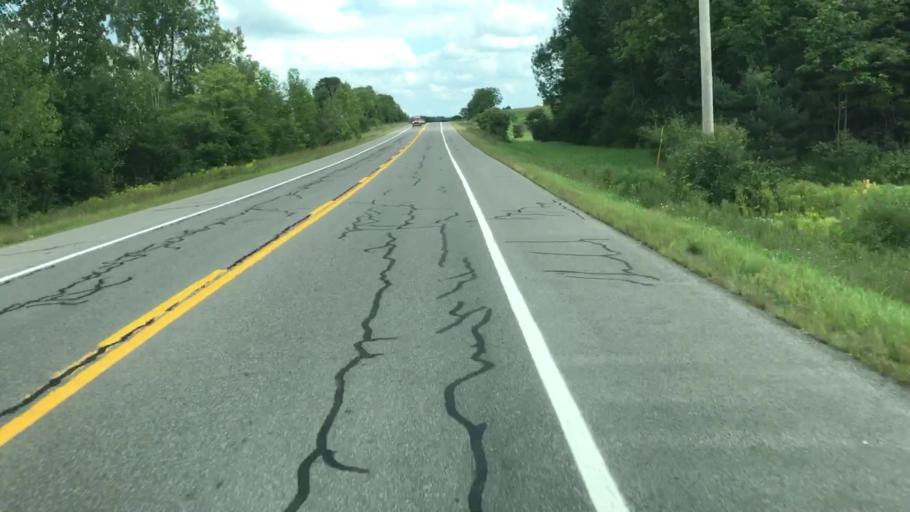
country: US
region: New York
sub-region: Onondaga County
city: Skaneateles
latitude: 42.9468
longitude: -76.3831
